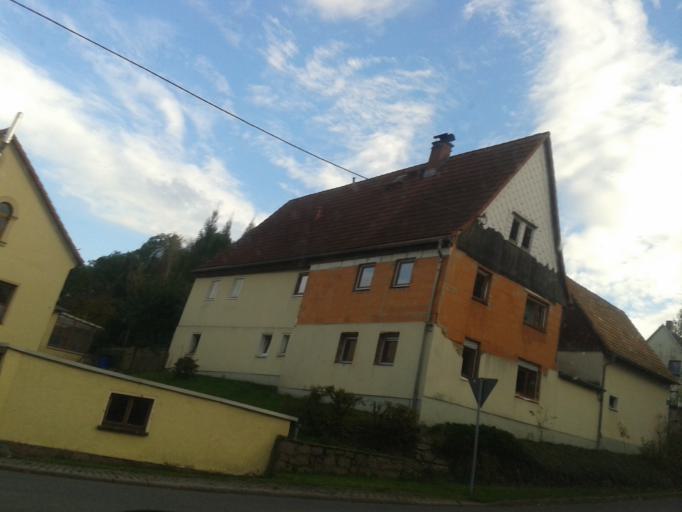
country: DE
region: Saxony
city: Reinsberg
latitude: 51.0100
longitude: 13.3581
